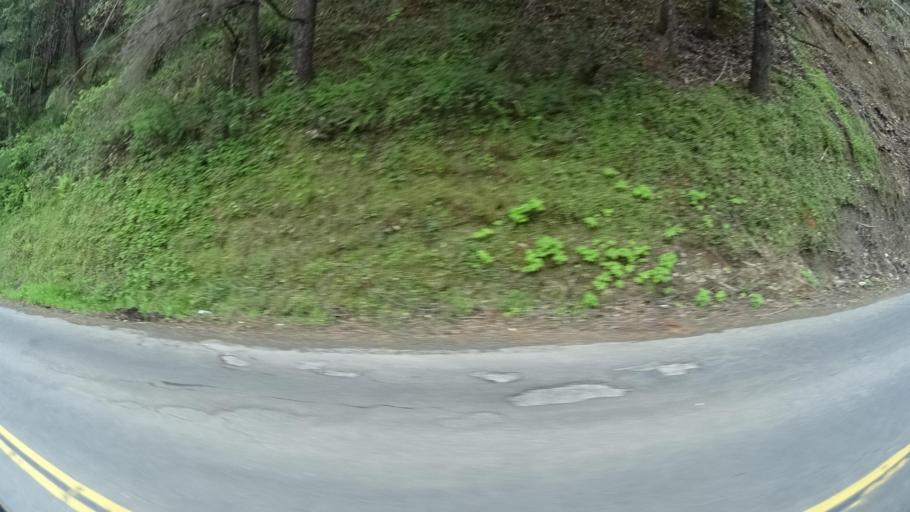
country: US
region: California
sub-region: Humboldt County
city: Willow Creek
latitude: 40.9414
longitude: -123.6239
